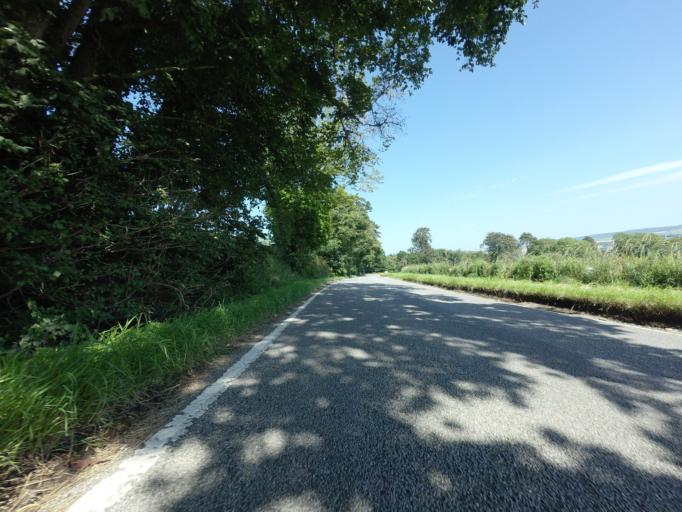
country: GB
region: Scotland
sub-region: Highland
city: Dingwall
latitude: 57.6202
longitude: -4.4011
